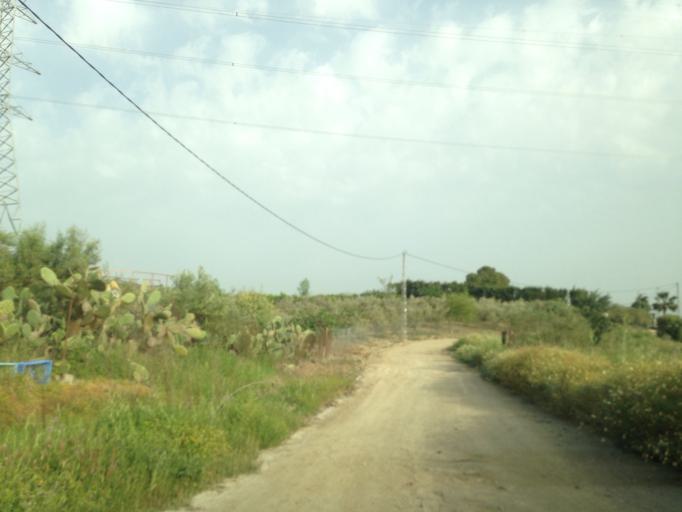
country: ES
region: Andalusia
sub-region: Provincia de Malaga
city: Estacion de Cartama
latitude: 36.7542
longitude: -4.5548
